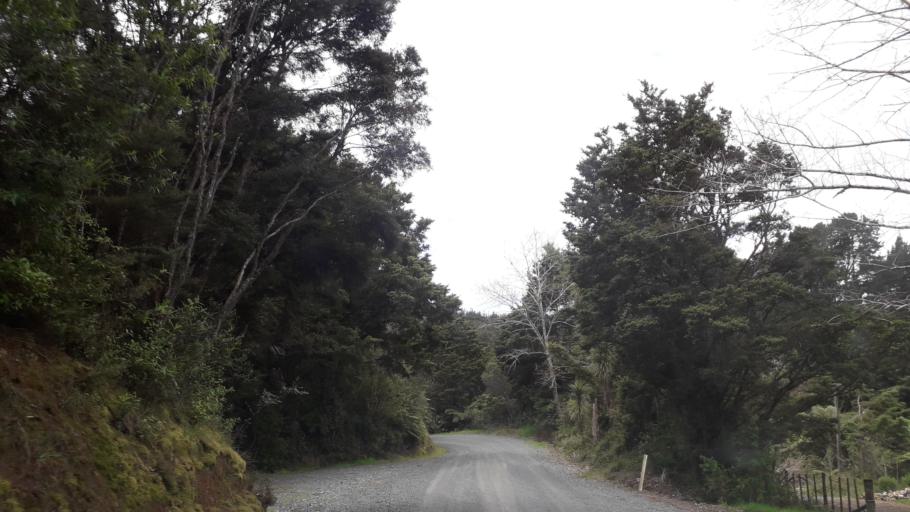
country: NZ
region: Northland
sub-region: Far North District
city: Taipa
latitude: -35.0732
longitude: 173.5543
